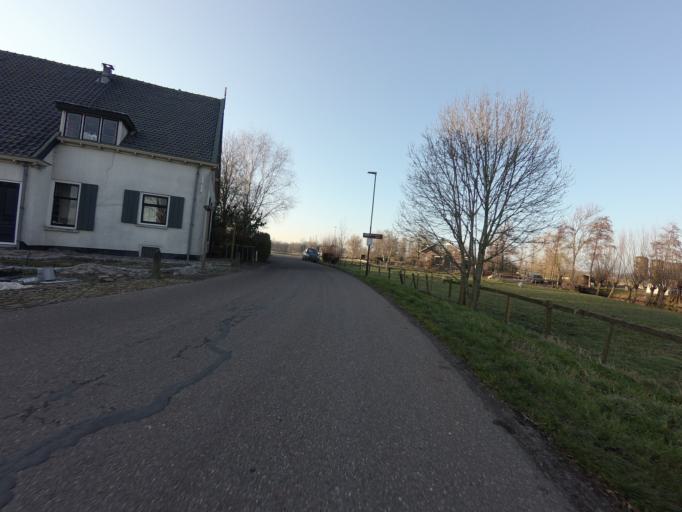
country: NL
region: South Holland
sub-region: Gemeente Giessenlanden
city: Giessenburg
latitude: 51.8868
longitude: 4.9346
